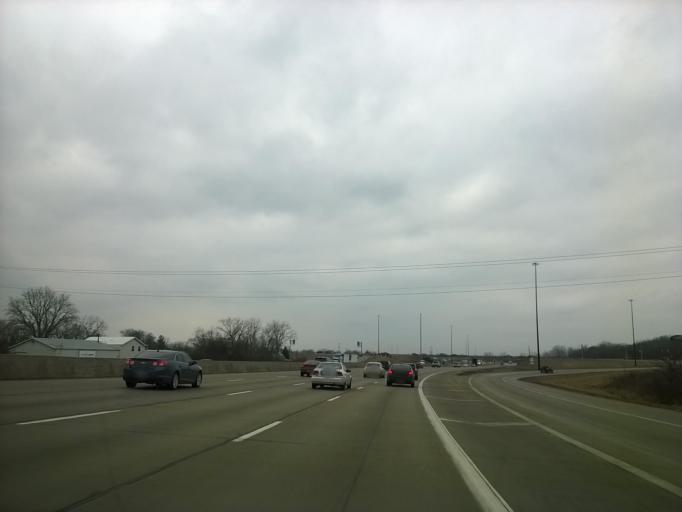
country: US
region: Indiana
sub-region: Marion County
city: Warren Park
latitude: 39.8028
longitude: -86.0783
